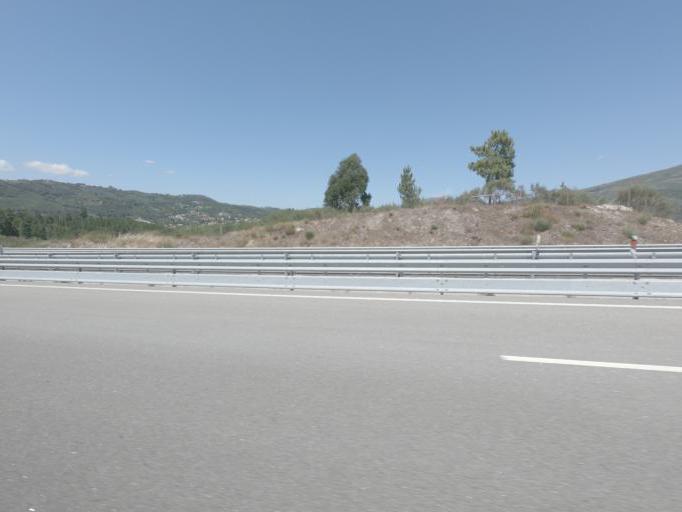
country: PT
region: Porto
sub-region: Amarante
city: Amarante
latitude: 41.2605
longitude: -8.0054
